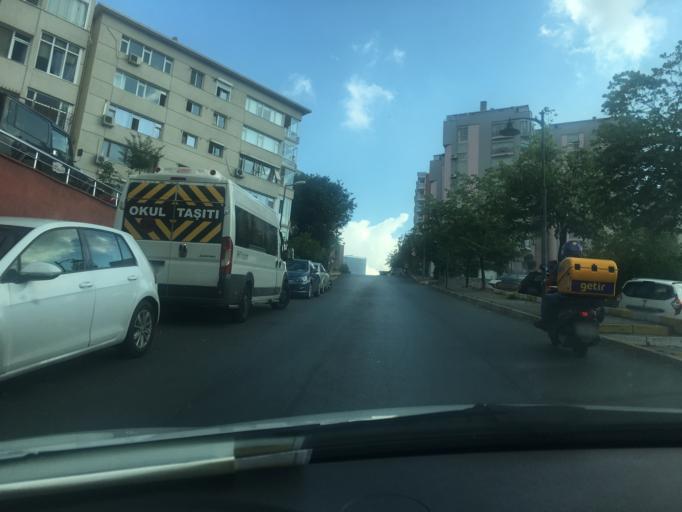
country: TR
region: Istanbul
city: Sisli
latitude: 41.0574
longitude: 28.9982
